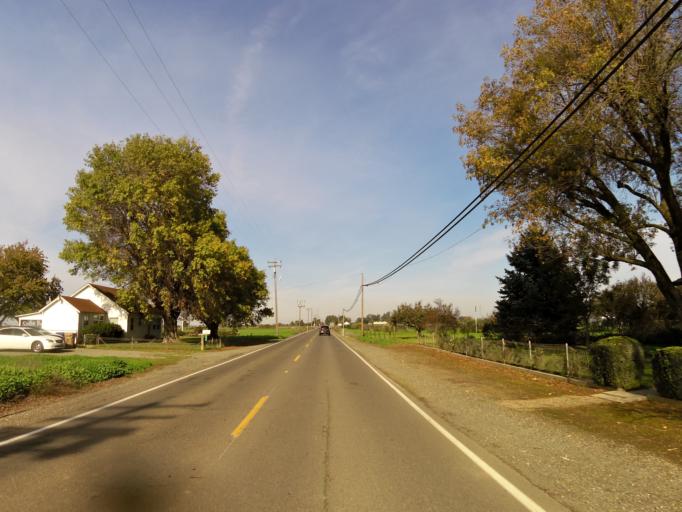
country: US
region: California
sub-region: Sacramento County
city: Laguna
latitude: 38.3471
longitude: -121.4175
